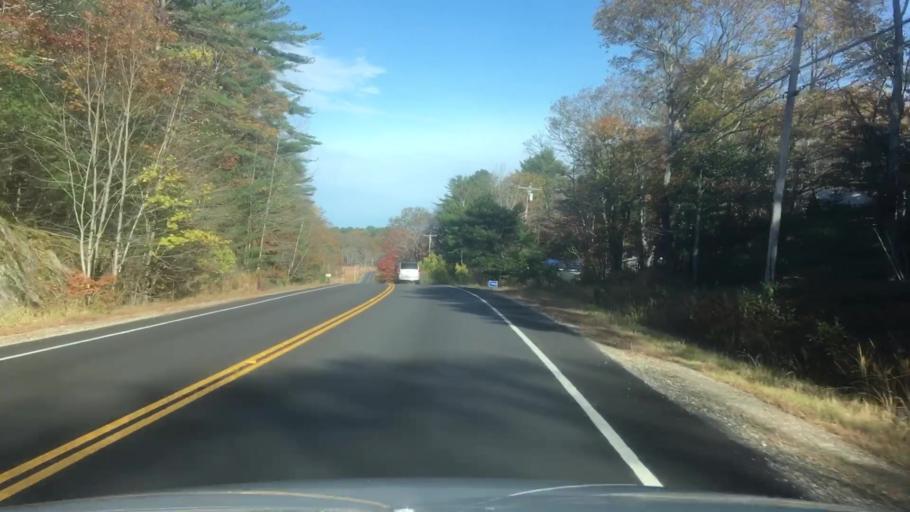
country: US
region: Maine
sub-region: Sagadahoc County
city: Woolwich
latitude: 43.8975
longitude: -69.7950
